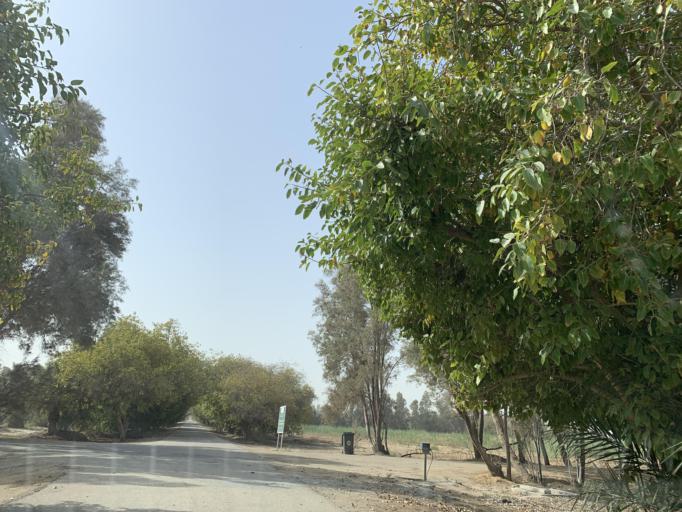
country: BH
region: Northern
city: Madinat `Isa
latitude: 26.1666
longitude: 50.5297
